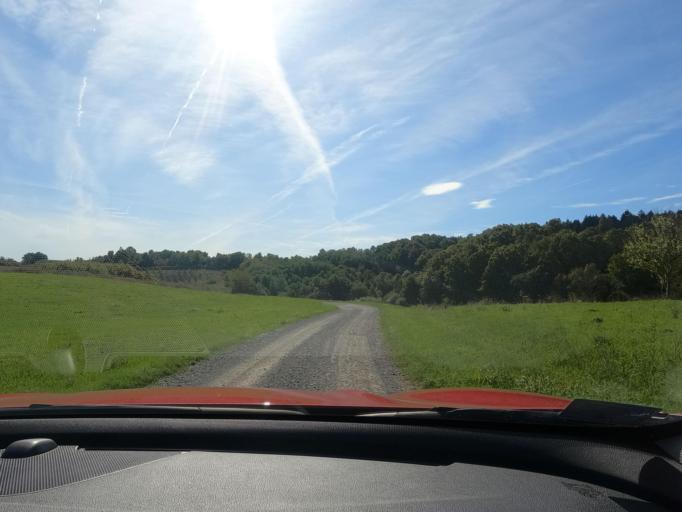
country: HR
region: Sisacko-Moslavacka
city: Petrinja
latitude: 45.3398
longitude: 16.2440
